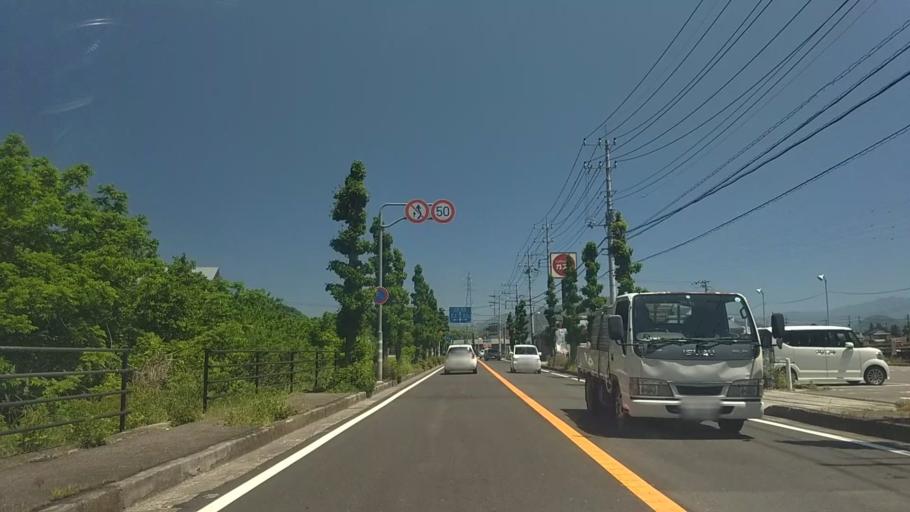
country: JP
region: Yamanashi
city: Nirasaki
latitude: 35.7849
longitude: 138.4179
